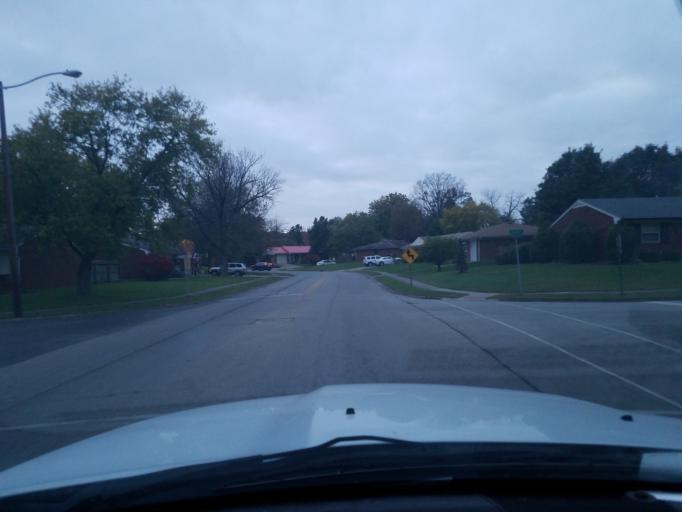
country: US
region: Indiana
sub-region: Floyd County
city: New Albany
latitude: 38.3042
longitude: -85.8309
